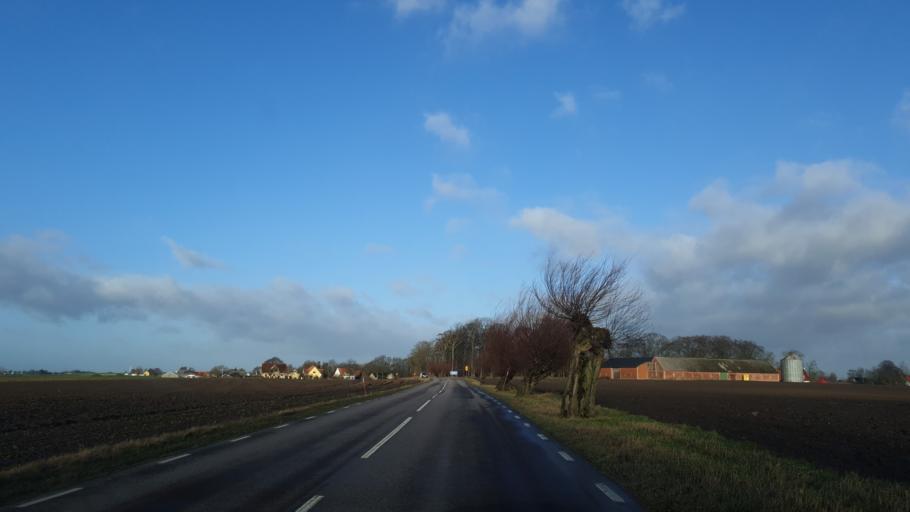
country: SE
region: Skane
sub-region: Vellinge Kommun
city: Vellinge
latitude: 55.4957
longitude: 13.0279
